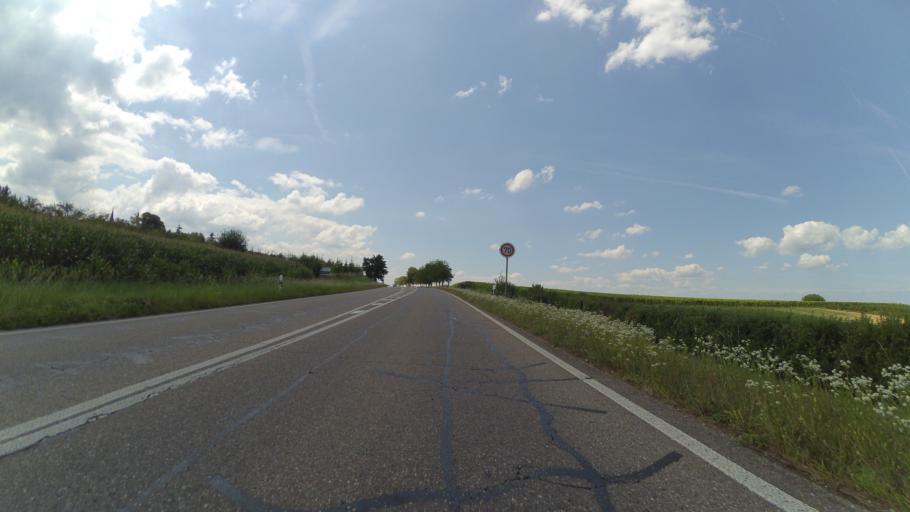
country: DE
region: Baden-Wuerttemberg
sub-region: Freiburg Region
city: Sulzburg
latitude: 47.8633
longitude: 7.6988
